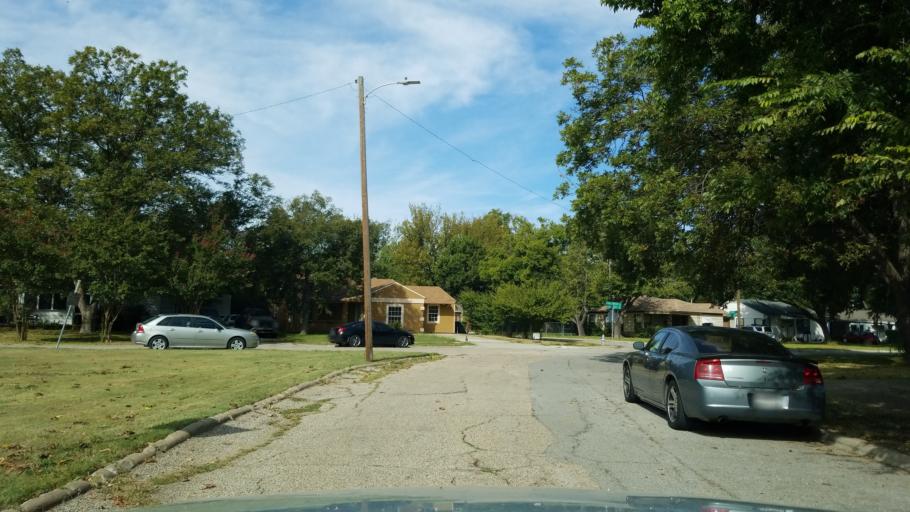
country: US
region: Texas
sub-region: Dallas County
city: Garland
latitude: 32.9015
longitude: -96.6515
